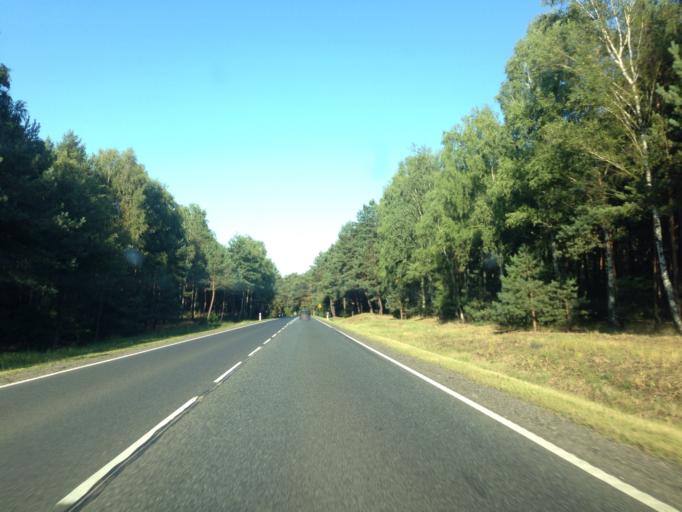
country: PL
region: Kujawsko-Pomorskie
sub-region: Powiat bydgoski
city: Nowa Wies Wielka
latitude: 53.0652
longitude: 18.1164
